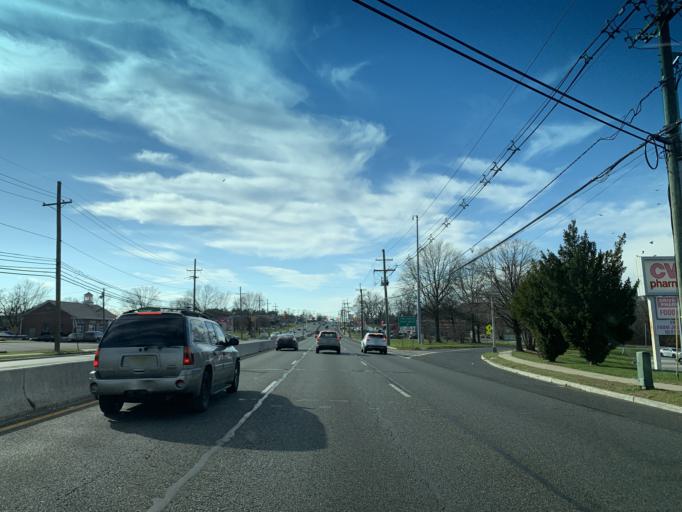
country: US
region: New Jersey
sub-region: Burlington County
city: Cinnaminson
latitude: 40.0118
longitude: -74.9629
